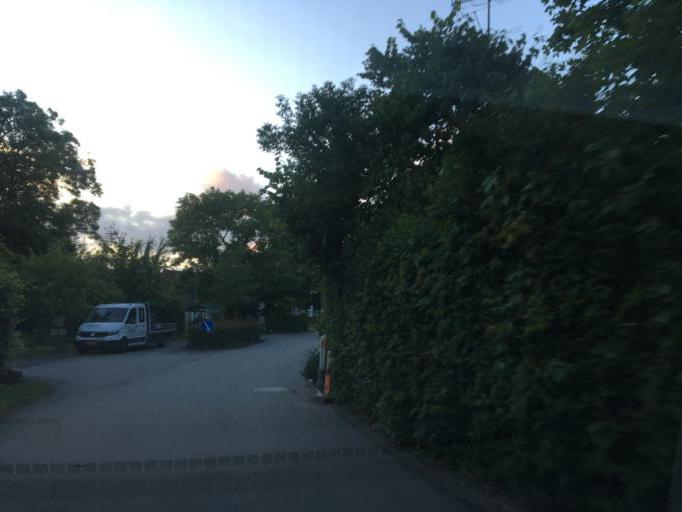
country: DK
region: Zealand
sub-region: Koge Kommune
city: Ejby
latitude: 55.5170
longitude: 12.0759
